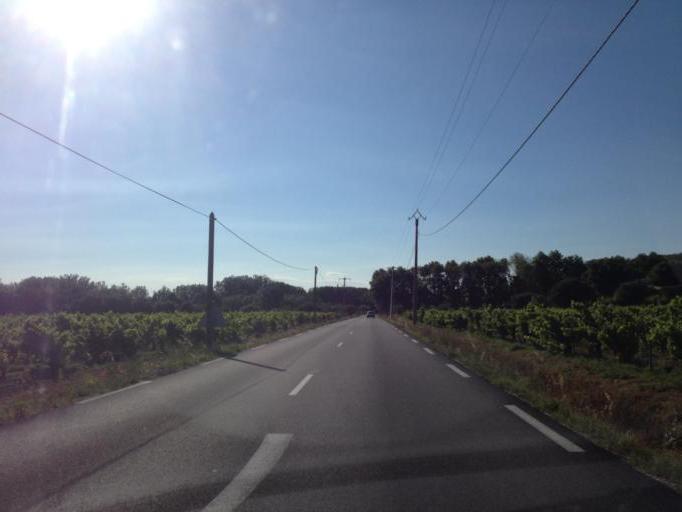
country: FR
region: Languedoc-Roussillon
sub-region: Departement du Gard
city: Roquemaure
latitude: 44.0604
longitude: 4.8010
